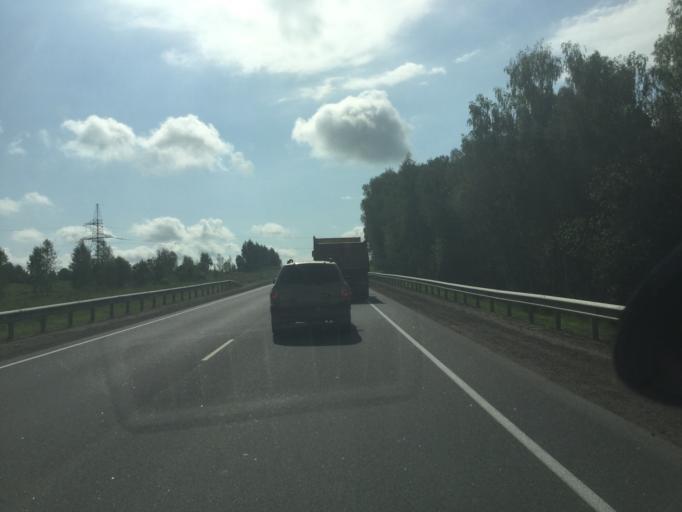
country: RU
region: Smolensk
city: Katyn'
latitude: 54.7538
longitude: 31.8645
